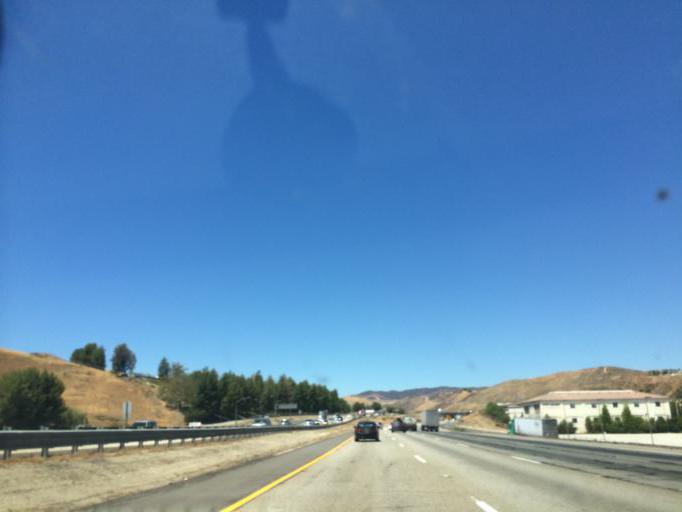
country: US
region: California
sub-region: Los Angeles County
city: Castaic
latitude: 34.4964
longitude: -118.6241
